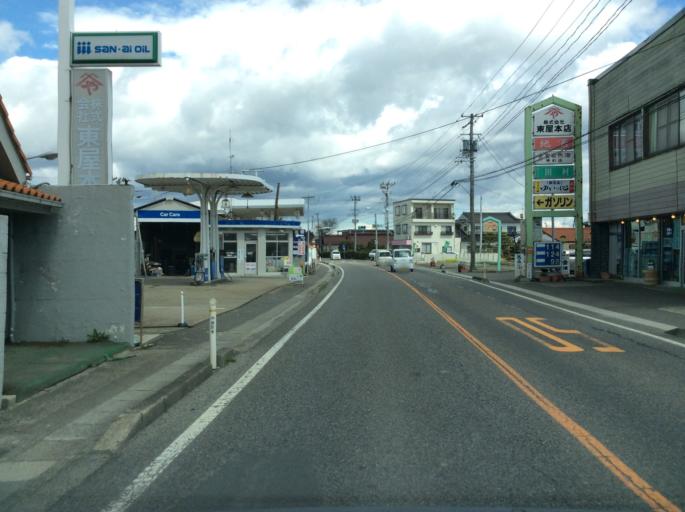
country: JP
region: Fukushima
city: Koriyama
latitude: 37.3599
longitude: 140.3966
